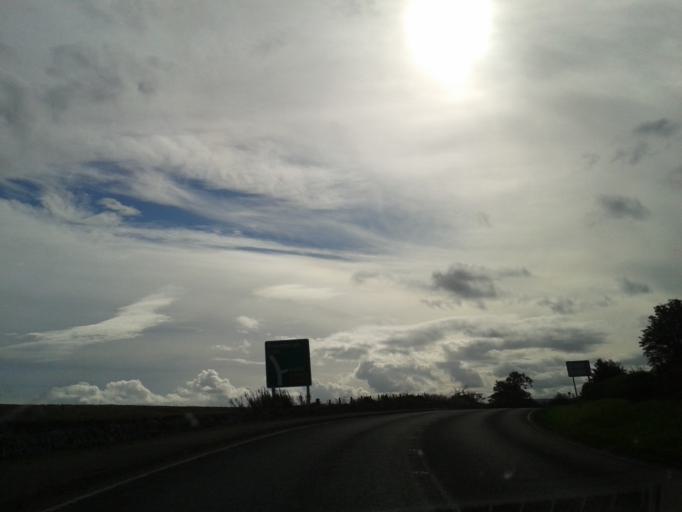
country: GB
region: Scotland
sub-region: Moray
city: Cullen
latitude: 57.6867
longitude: -2.8144
